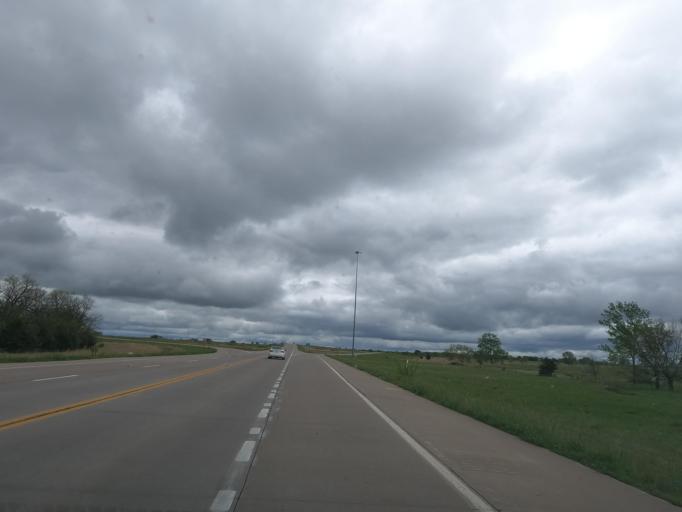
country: US
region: Kansas
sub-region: Montgomery County
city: Cherryvale
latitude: 37.3467
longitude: -95.5384
